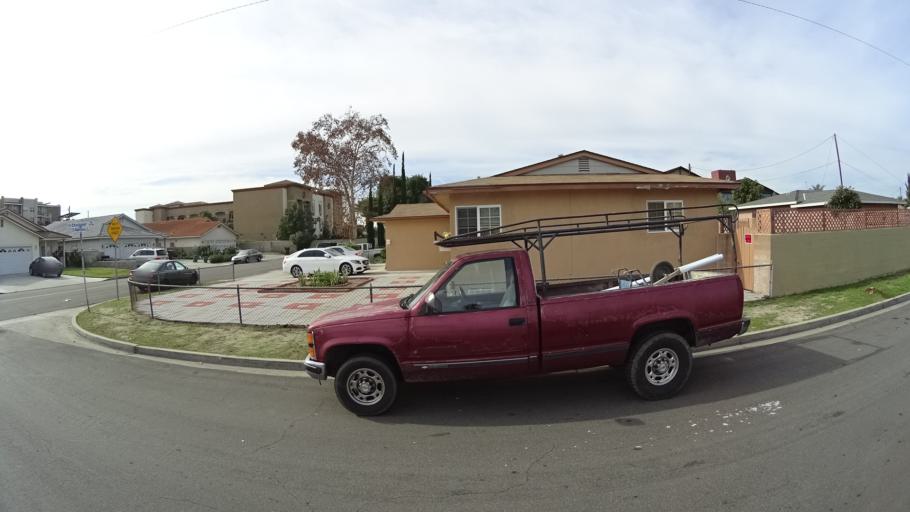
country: US
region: California
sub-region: Orange County
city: Garden Grove
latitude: 33.7777
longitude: -117.9137
